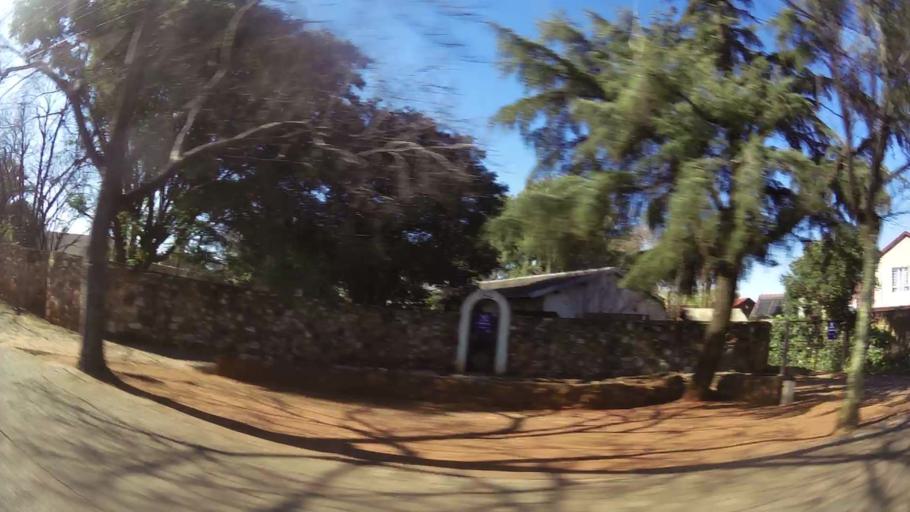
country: ZA
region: Gauteng
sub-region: City of Tshwane Metropolitan Municipality
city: Centurion
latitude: -25.8523
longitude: 28.2059
